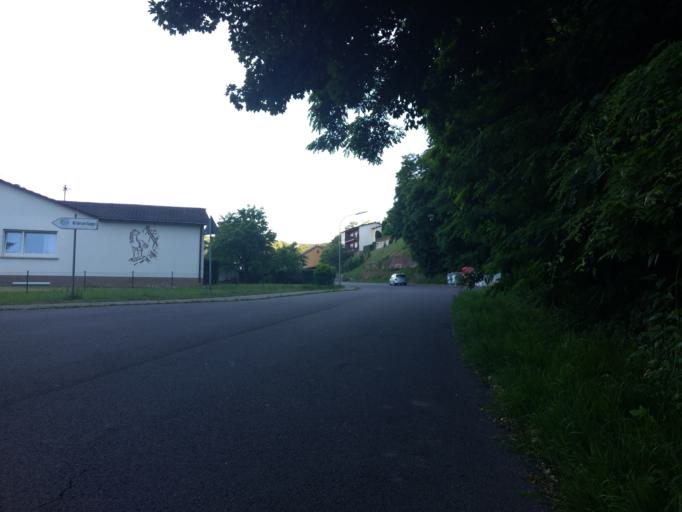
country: DE
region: Saarland
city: Merzig
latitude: 49.4215
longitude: 6.6304
